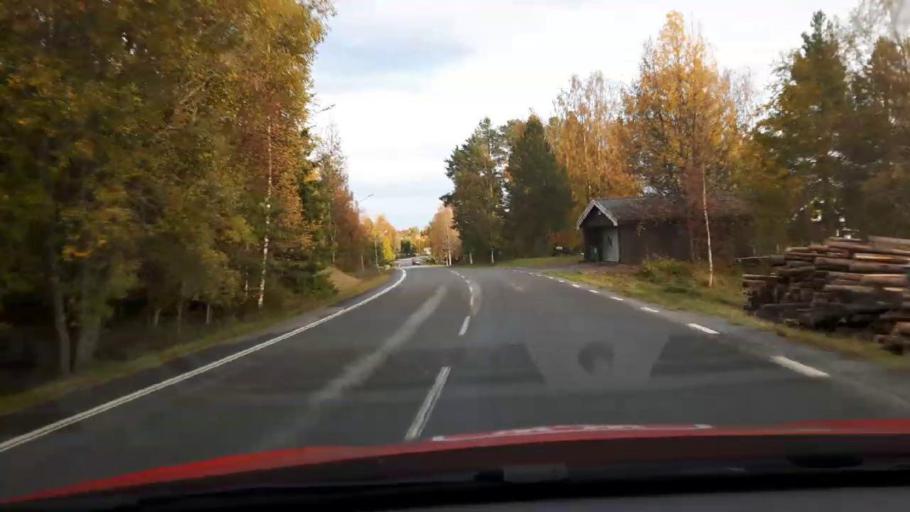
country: SE
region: Jaemtland
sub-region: Krokoms Kommun
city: Krokom
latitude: 63.3455
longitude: 14.5651
